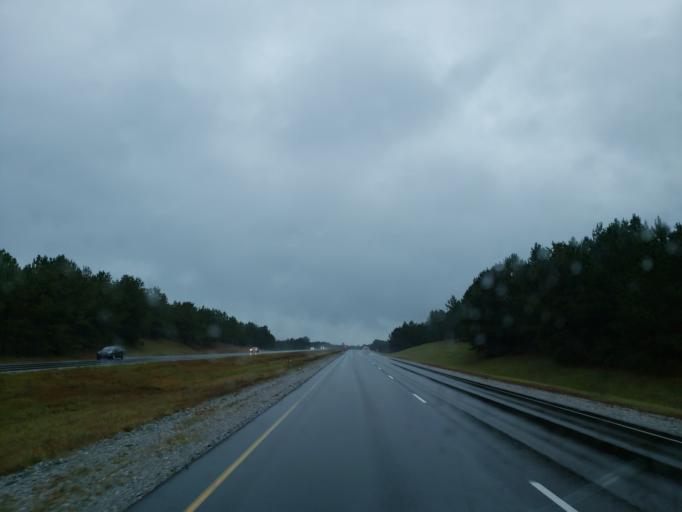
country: US
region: Mississippi
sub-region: Clarke County
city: Stonewall
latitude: 32.1381
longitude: -88.7139
